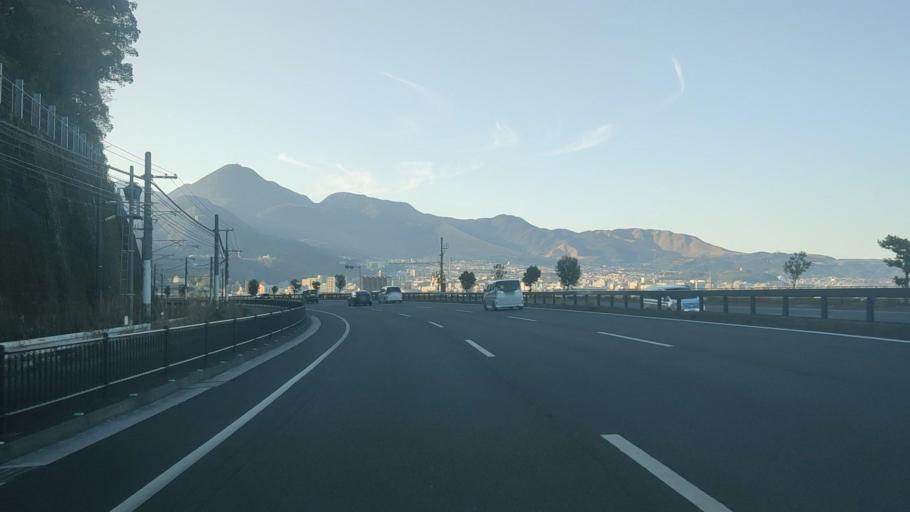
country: JP
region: Oita
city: Beppu
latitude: 33.2647
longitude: 131.5257
